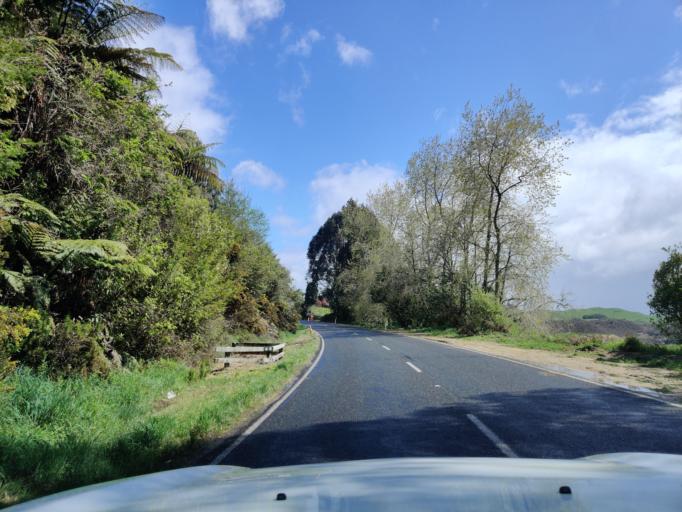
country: NZ
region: Bay of Plenty
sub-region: Rotorua District
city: Rotorua
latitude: -38.1754
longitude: 176.3255
